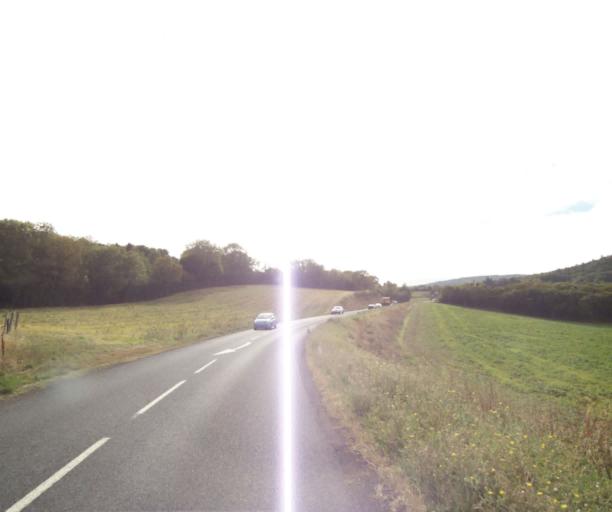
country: FR
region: Auvergne
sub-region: Departement du Puy-de-Dome
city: Ceyrat
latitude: 45.7129
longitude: 3.0776
